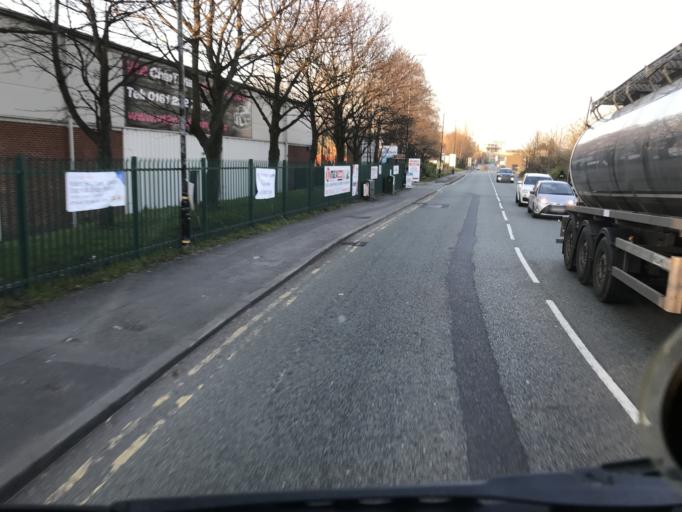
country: GB
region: England
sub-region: City and Borough of Salford
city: Eccles
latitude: 53.4735
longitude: -2.3343
